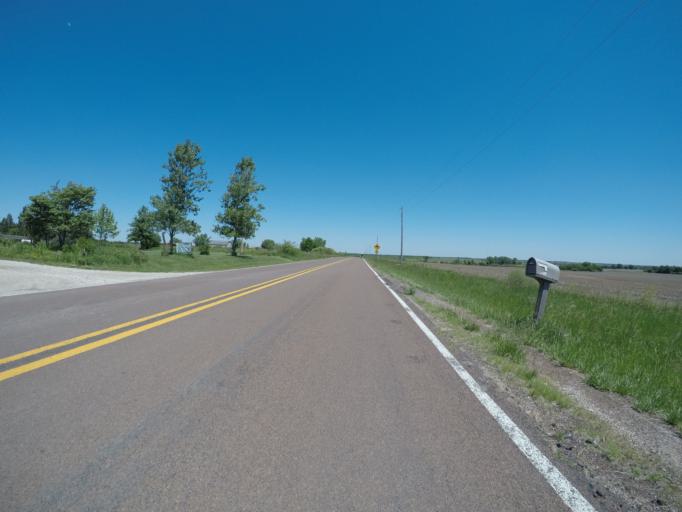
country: US
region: Kansas
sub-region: Shawnee County
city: Auburn
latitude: 38.9252
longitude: -95.9280
